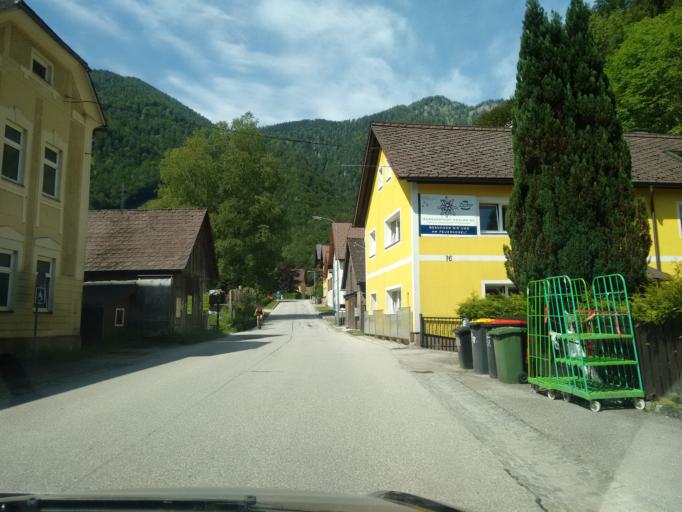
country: AT
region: Upper Austria
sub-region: Politischer Bezirk Gmunden
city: Ebensee
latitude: 47.8143
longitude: 13.7630
